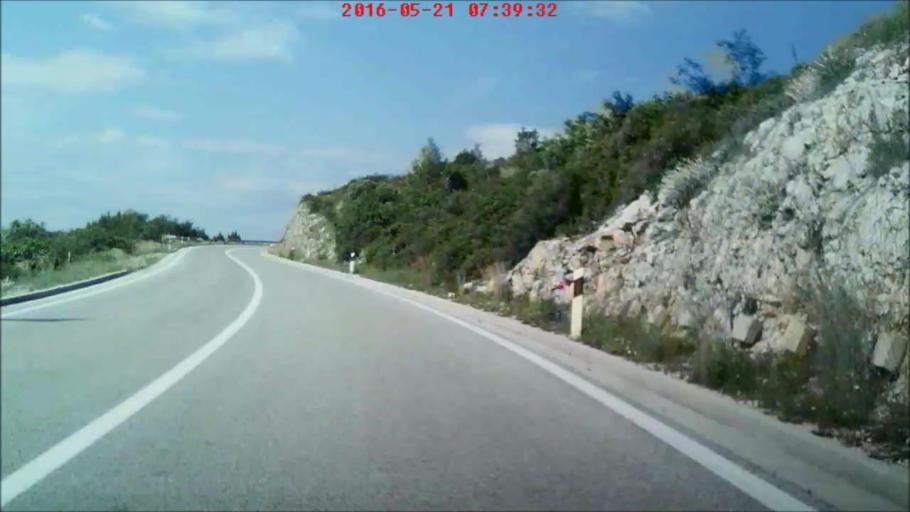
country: HR
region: Dubrovacko-Neretvanska
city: Podgora
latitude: 42.8050
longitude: 17.8385
